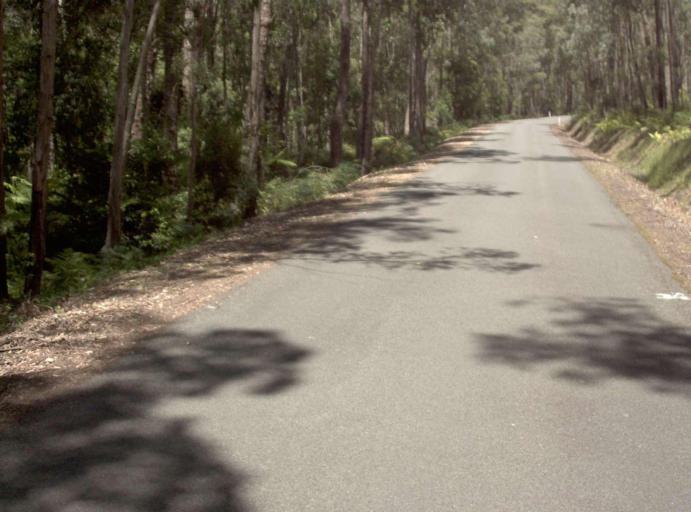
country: AU
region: New South Wales
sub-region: Bombala
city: Bombala
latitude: -37.4850
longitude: 148.9297
